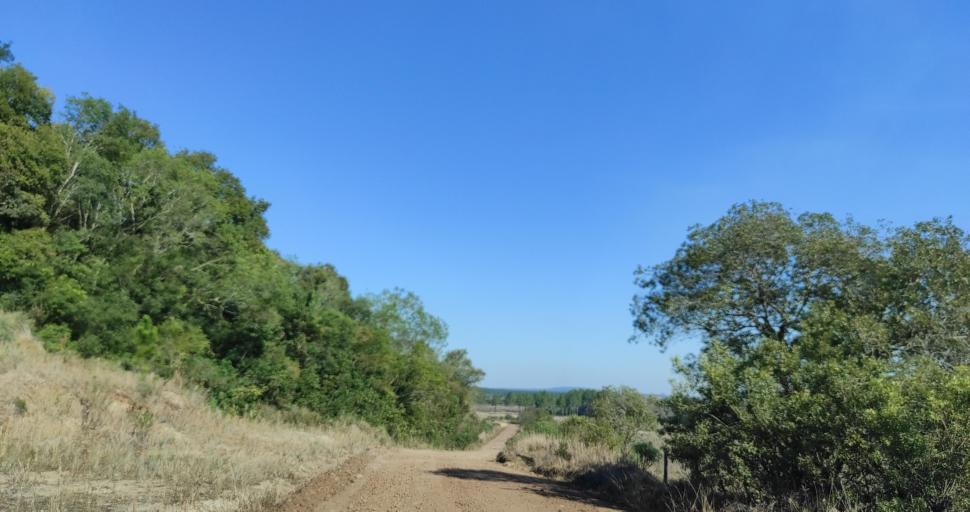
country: AR
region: Misiones
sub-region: Departamento de Apostoles
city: San Jose
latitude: -27.6709
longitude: -55.6613
